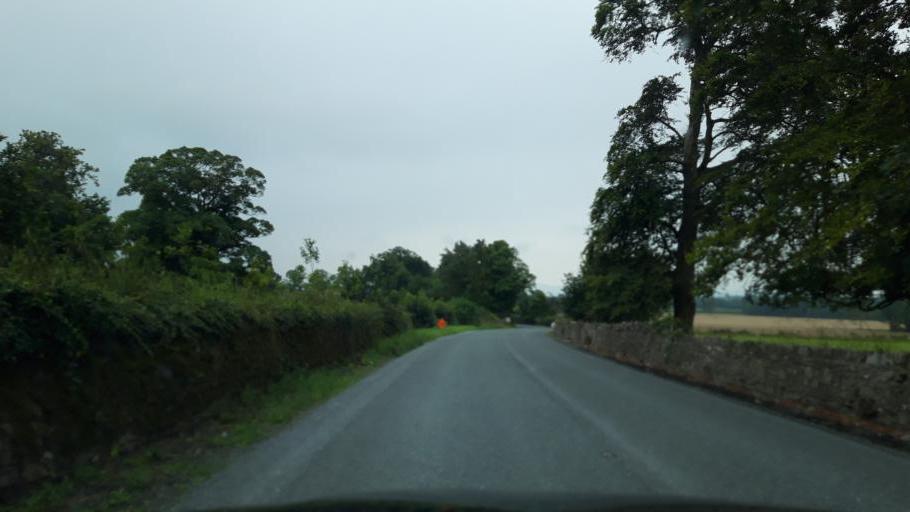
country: IE
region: Munster
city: Fethard
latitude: 52.4362
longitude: -7.6992
